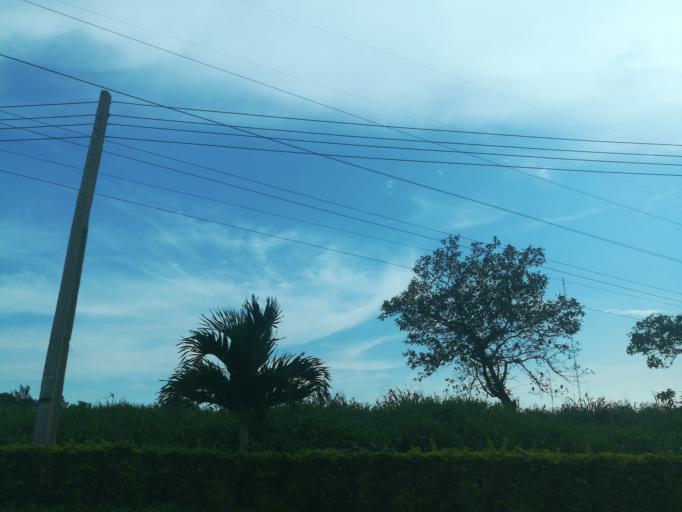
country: NG
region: Lagos
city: Ikorodu
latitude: 6.6364
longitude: 3.5346
